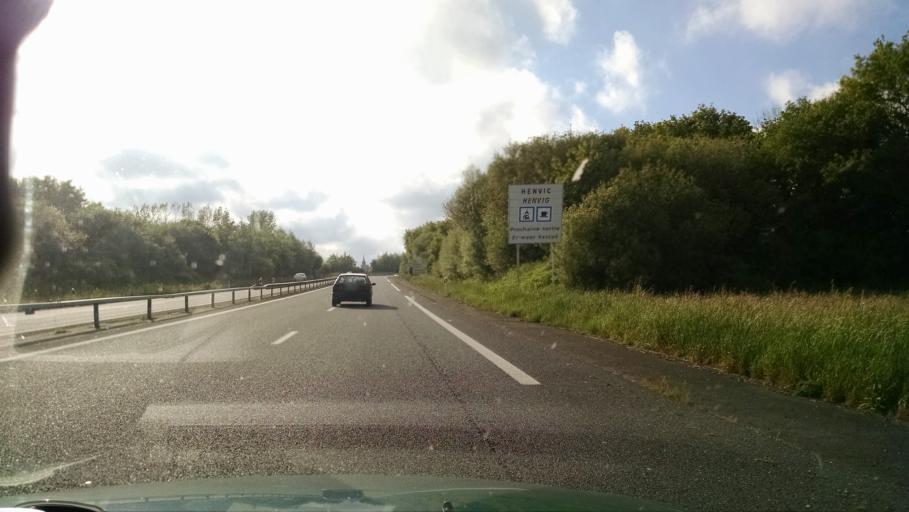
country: FR
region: Brittany
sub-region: Departement du Finistere
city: Henvic
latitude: 48.6286
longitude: -3.9151
